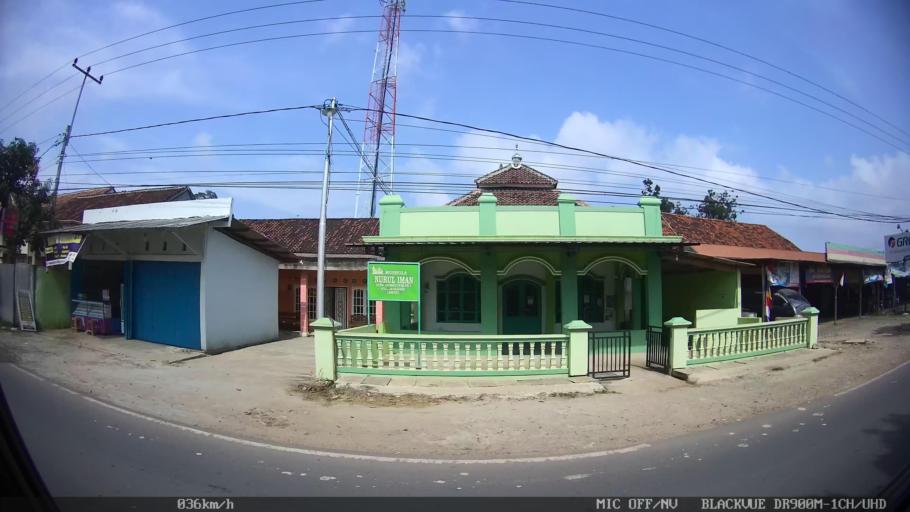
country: ID
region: Lampung
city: Kedaton
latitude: -5.3254
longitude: 105.2896
